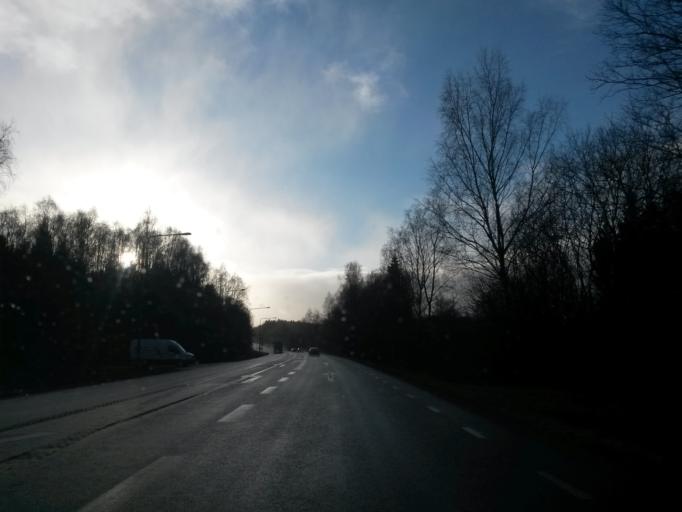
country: SE
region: Vaestra Goetaland
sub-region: Boras Kommun
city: Boras
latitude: 57.7736
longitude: 12.9770
